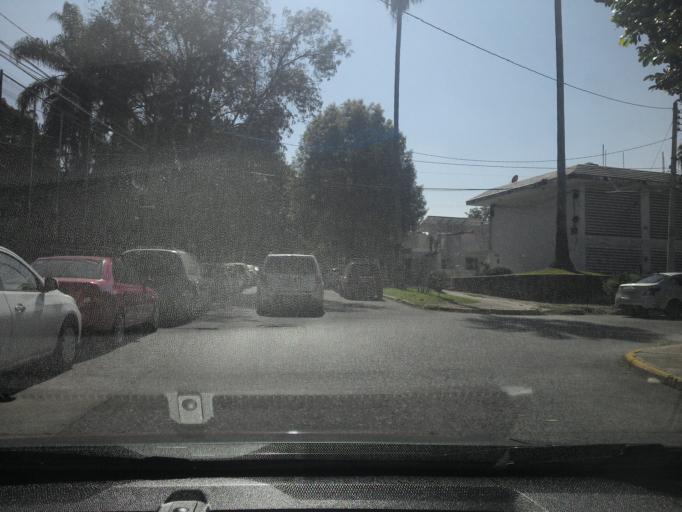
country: MX
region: Jalisco
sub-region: Zapopan
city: Zapopan
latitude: 20.7014
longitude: -103.3784
